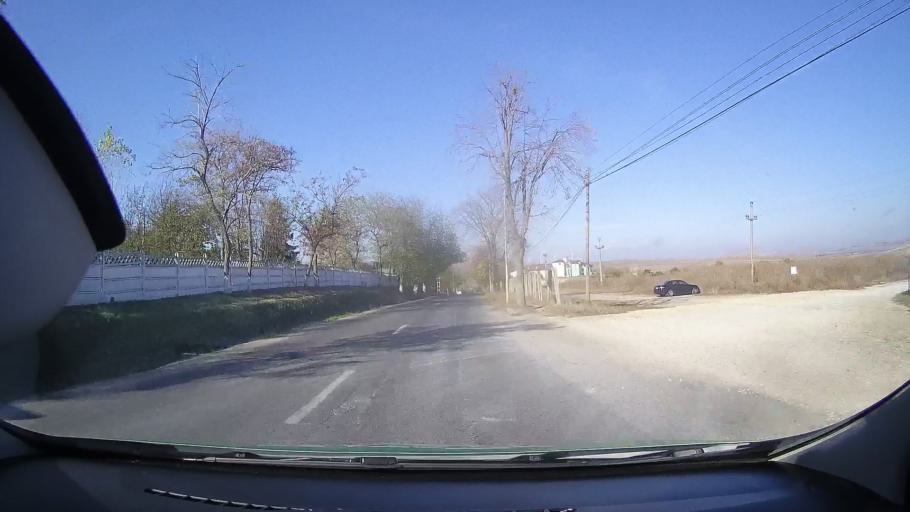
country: RO
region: Tulcea
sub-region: Oras Babadag
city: Babadag
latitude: 44.8860
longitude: 28.7353
